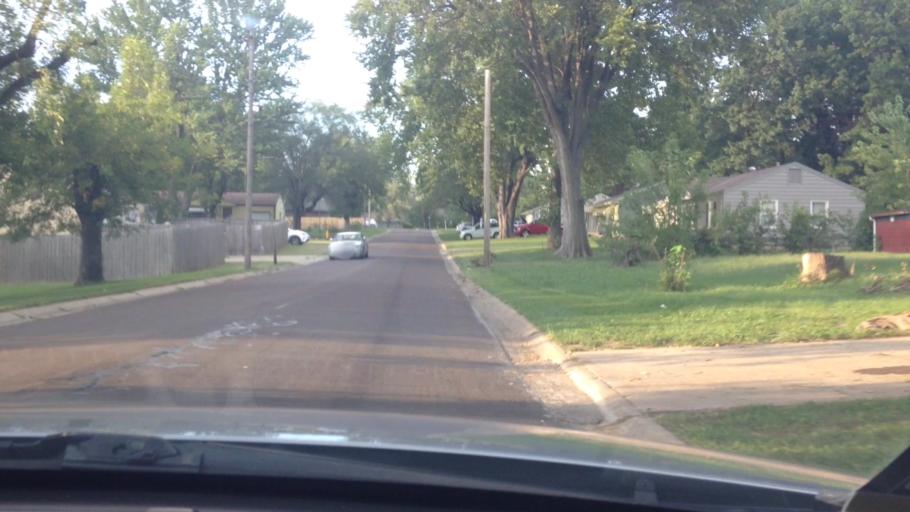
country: US
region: Missouri
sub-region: Jackson County
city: Raytown
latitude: 38.9663
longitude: -94.4883
